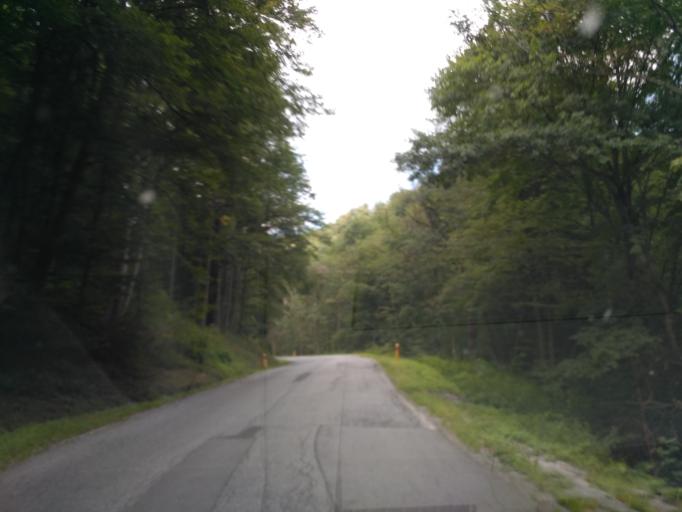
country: SK
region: Kosicky
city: Gelnica
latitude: 48.9210
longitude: 21.0387
